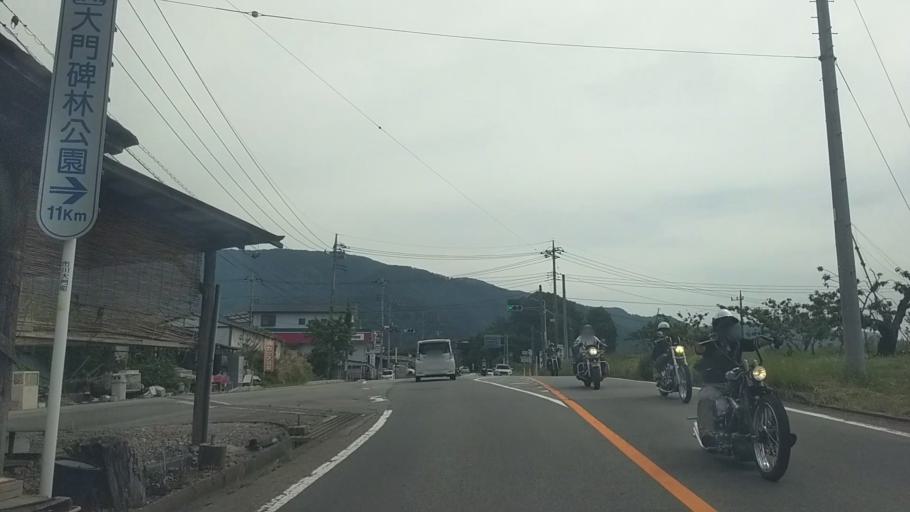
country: JP
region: Yamanashi
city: Isawa
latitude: 35.5751
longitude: 138.5915
